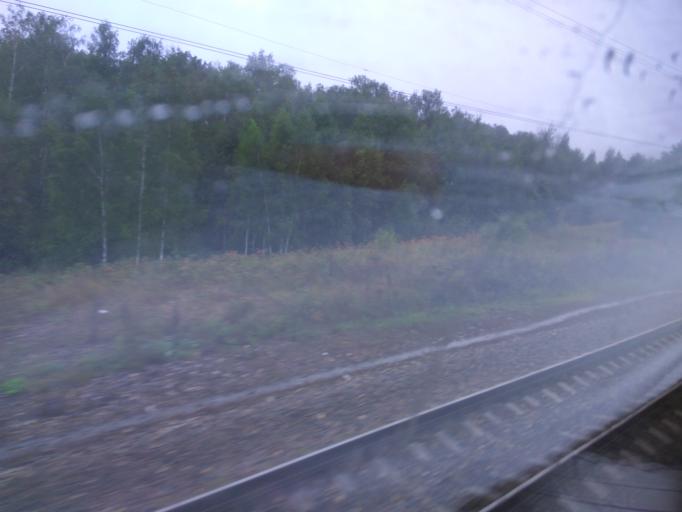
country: RU
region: Moskovskaya
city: Zhilevo
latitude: 54.9967
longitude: 38.0255
